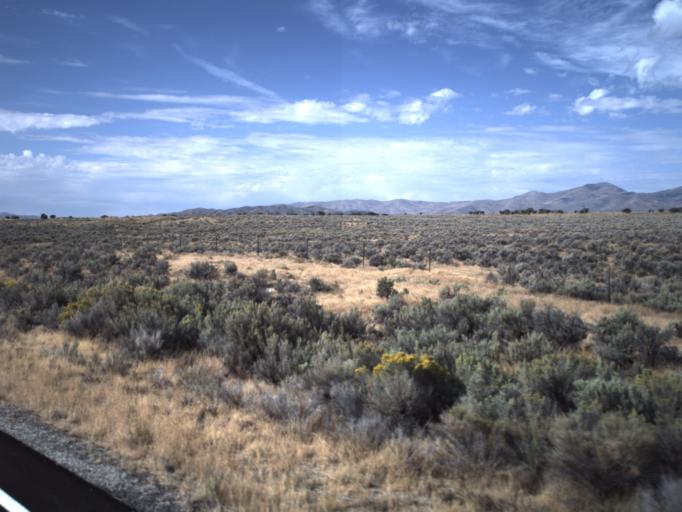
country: US
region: Idaho
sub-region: Cassia County
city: Burley
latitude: 41.7166
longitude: -113.5280
